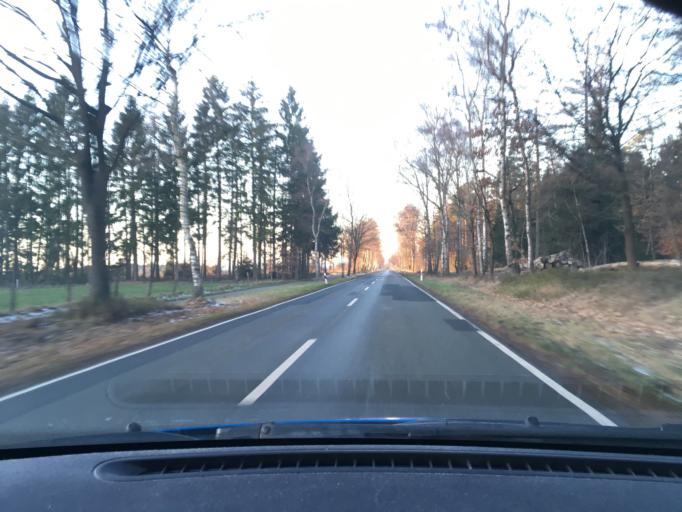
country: DE
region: Lower Saxony
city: Undeloh
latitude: 53.2098
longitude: 9.9542
